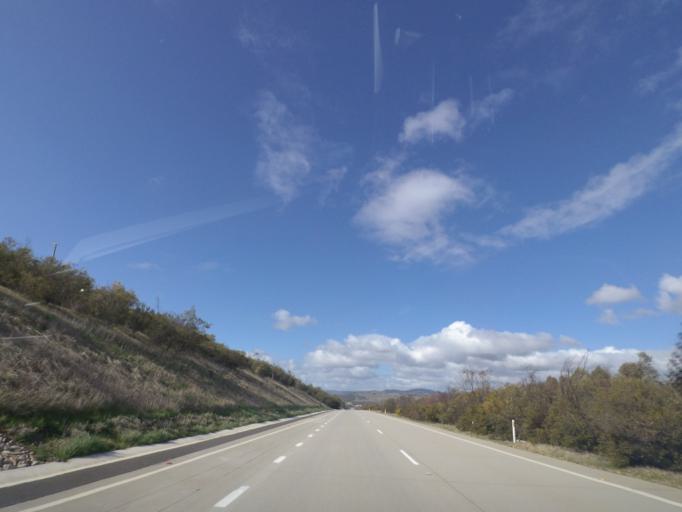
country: AU
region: New South Wales
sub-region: Albury Municipality
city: Lavington
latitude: -35.9153
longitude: 147.1083
